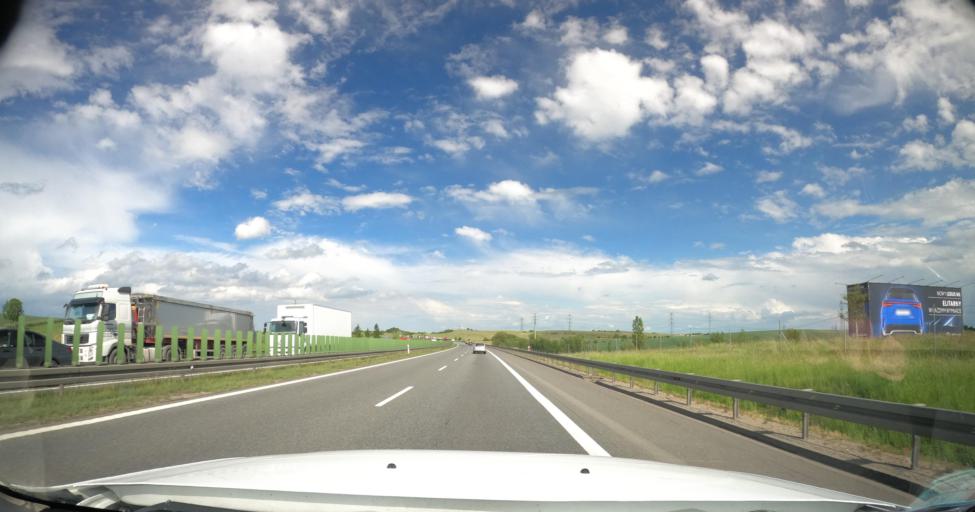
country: PL
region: Pomeranian Voivodeship
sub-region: Powiat gdanski
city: Rotmanka
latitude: 54.2890
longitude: 18.6023
